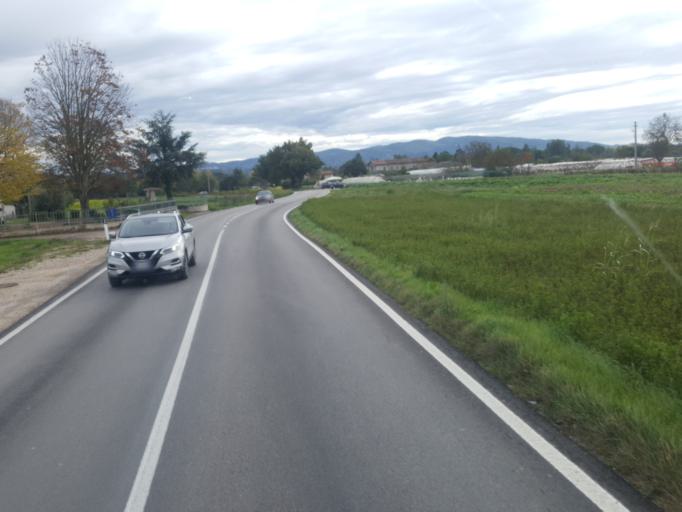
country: IT
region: Umbria
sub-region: Provincia di Perugia
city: San Martino in Campo
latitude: 43.0743
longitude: 12.4244
